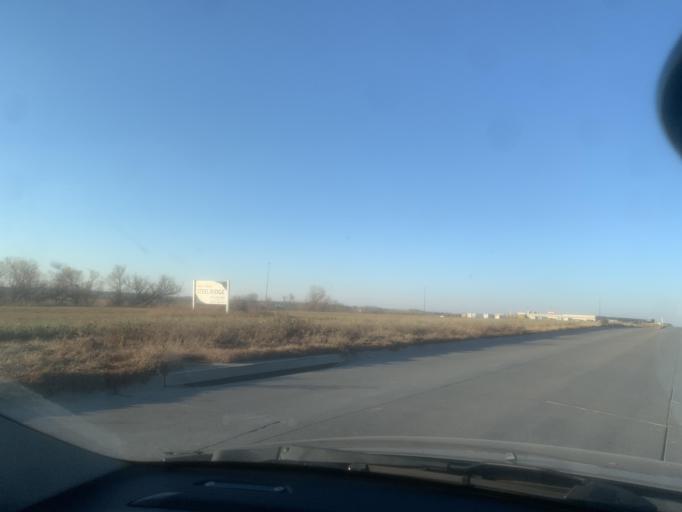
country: US
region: Nebraska
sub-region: Sarpy County
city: Chalco
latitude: 41.1388
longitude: -96.1580
